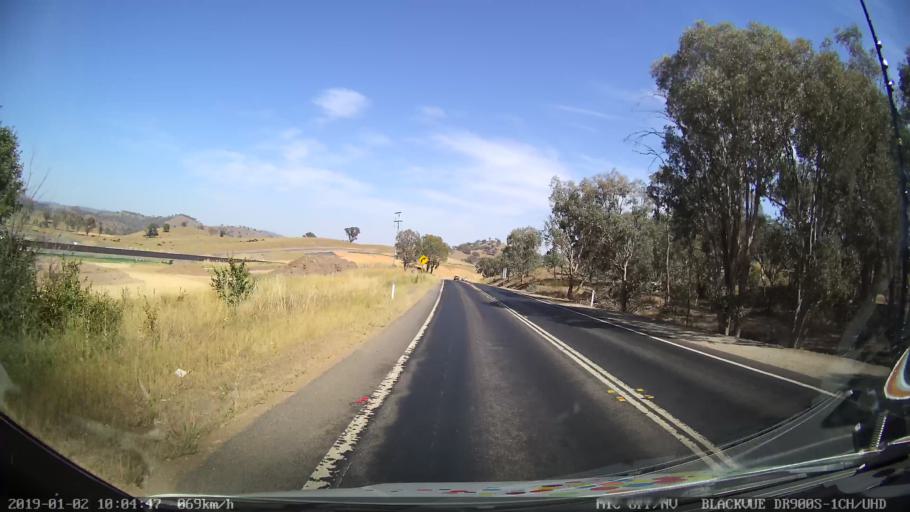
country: AU
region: New South Wales
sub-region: Gundagai
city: Gundagai
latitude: -35.1646
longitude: 148.1211
